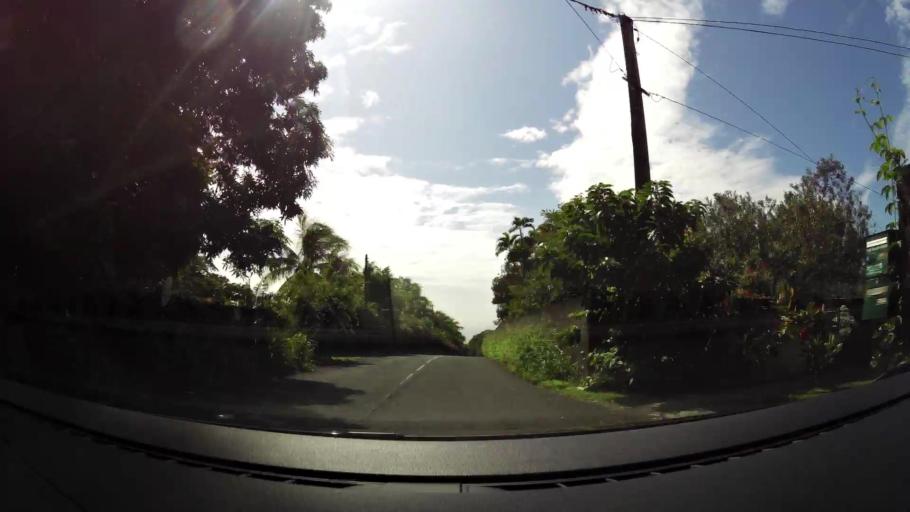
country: GP
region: Guadeloupe
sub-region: Guadeloupe
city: Basse-Terre
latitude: 16.0140
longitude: -61.7199
